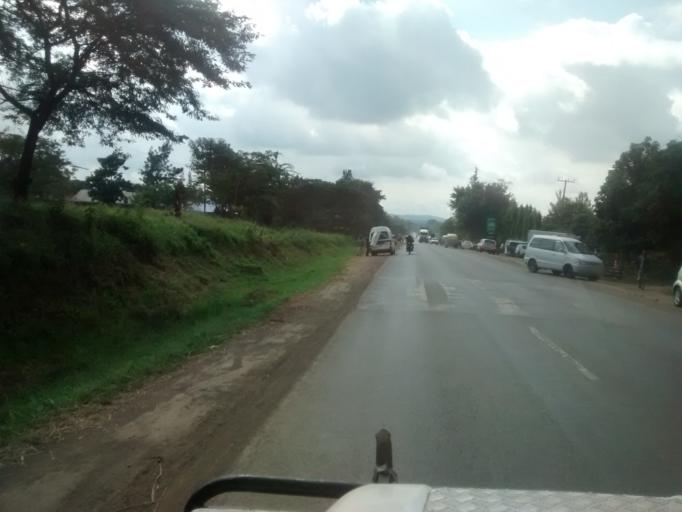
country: TZ
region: Arusha
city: Usa River
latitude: -3.3732
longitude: 36.8467
